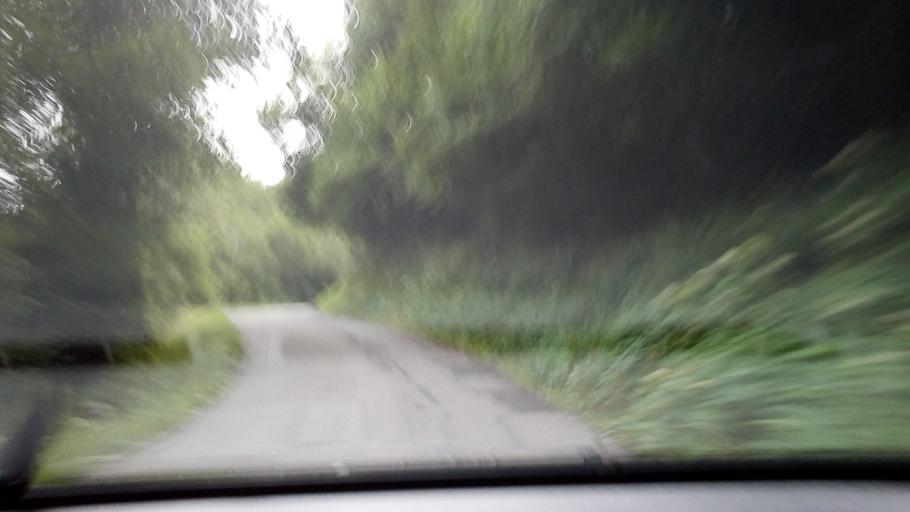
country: FR
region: Midi-Pyrenees
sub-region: Departement des Hautes-Pyrenees
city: Cauterets
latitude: 42.9511
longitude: -0.2057
